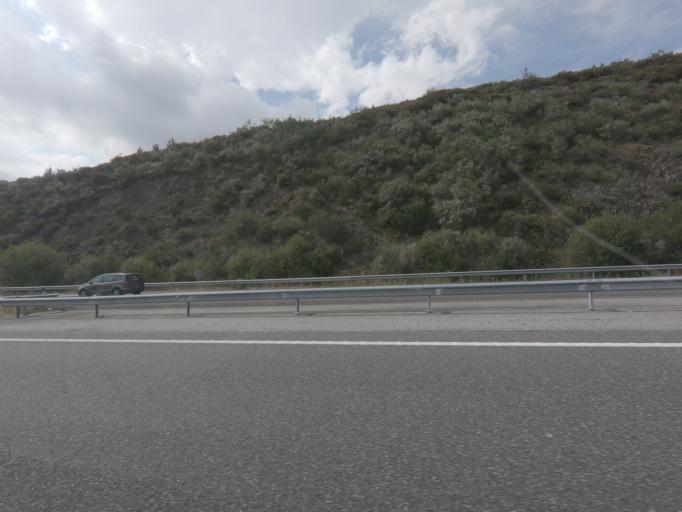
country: ES
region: Galicia
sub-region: Provincia de Ourense
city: Melon
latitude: 42.2272
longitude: -8.2385
